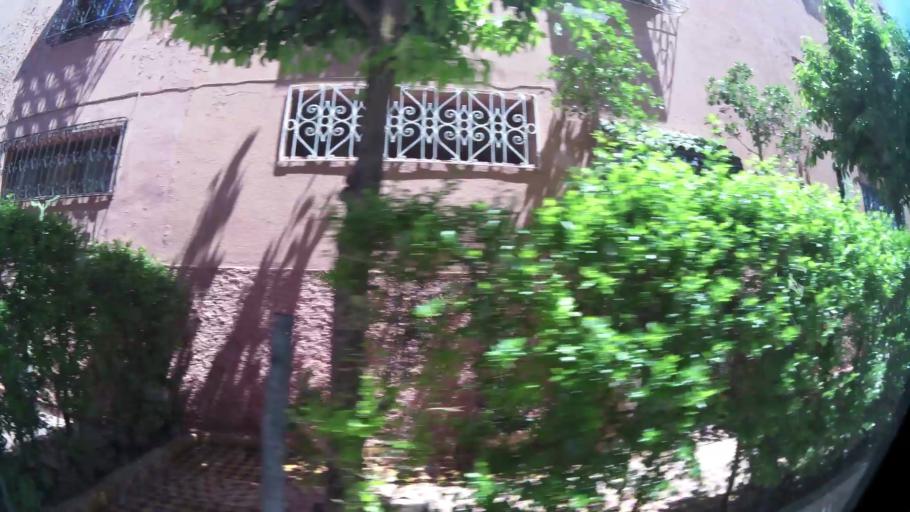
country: MA
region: Marrakech-Tensift-Al Haouz
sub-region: Marrakech
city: Marrakesh
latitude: 31.6528
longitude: -7.9994
